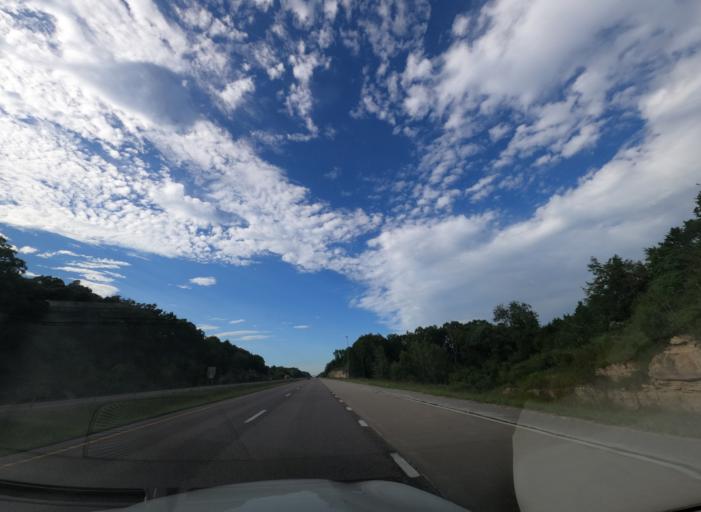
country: US
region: Missouri
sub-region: Jefferson County
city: Crystal City
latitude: 38.0963
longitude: -90.3017
